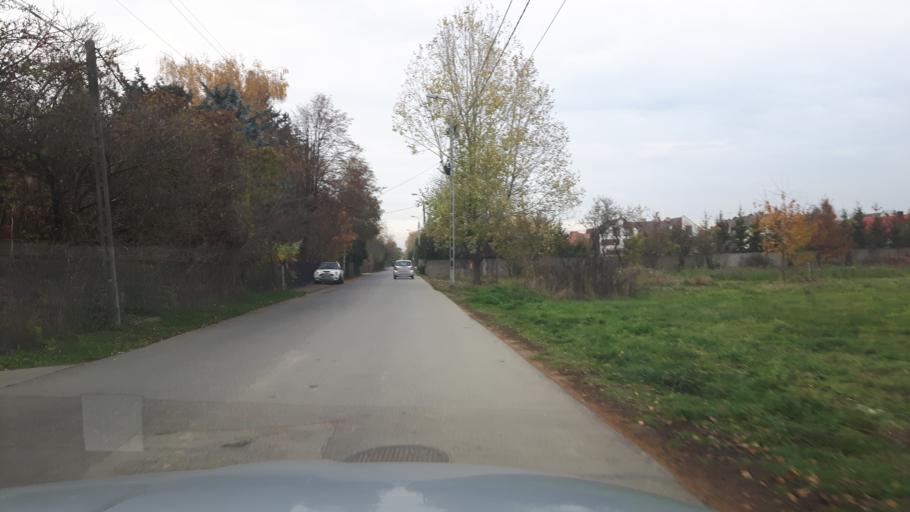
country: PL
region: Masovian Voivodeship
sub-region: Warszawa
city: Wilanow
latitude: 52.1663
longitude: 21.1182
